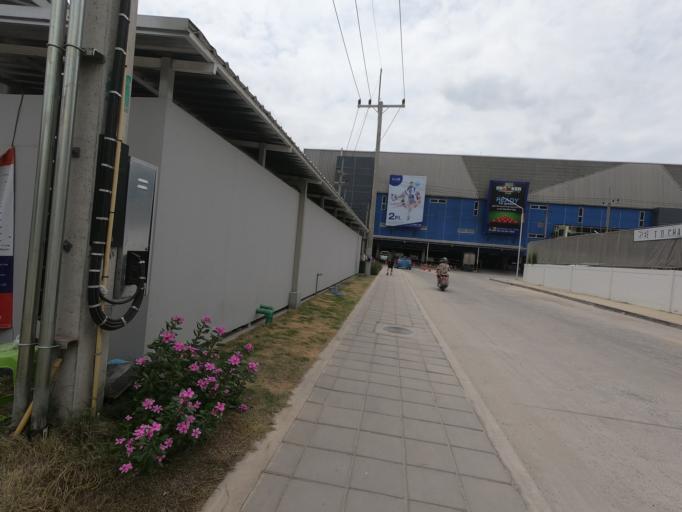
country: TH
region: Bangkok
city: Sai Mai
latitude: 13.9513
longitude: 100.6521
